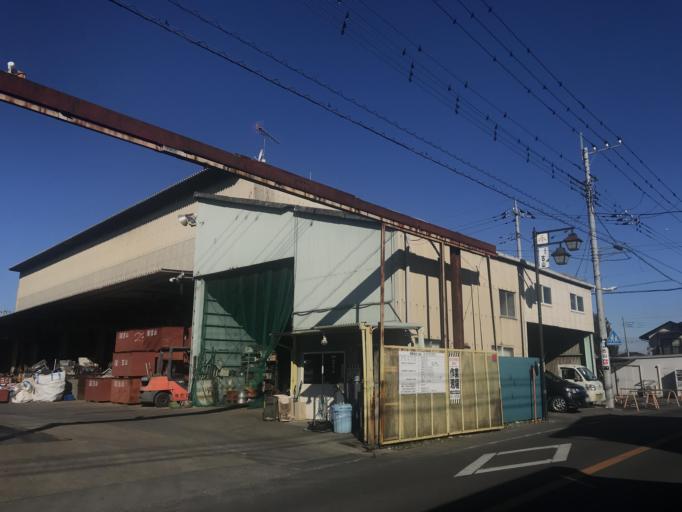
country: JP
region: Ibaraki
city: Yuki
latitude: 36.3068
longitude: 139.8746
